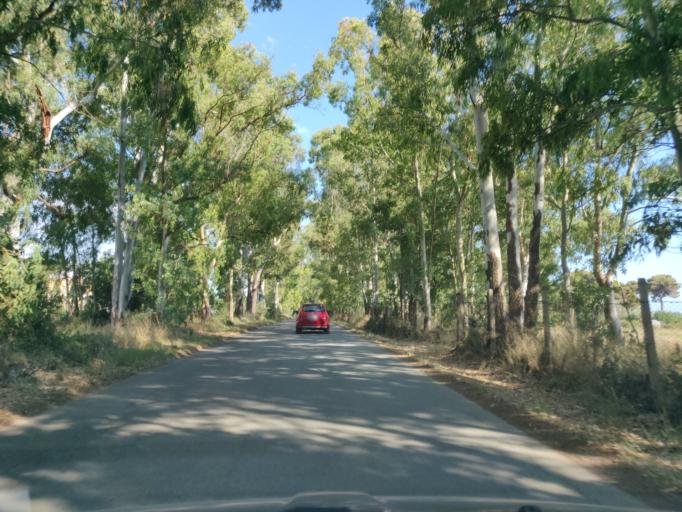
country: IT
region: Latium
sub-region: Citta metropolitana di Roma Capitale
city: Aurelia
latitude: 42.1648
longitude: 11.7427
